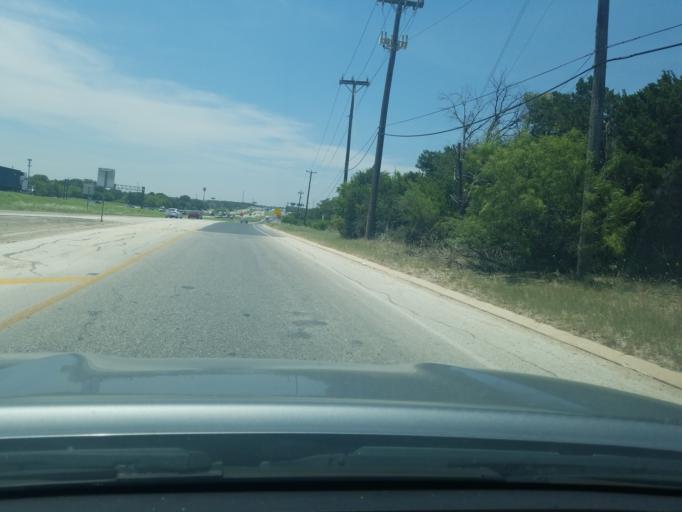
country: US
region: Texas
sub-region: Bexar County
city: Hollywood Park
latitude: 29.6020
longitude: -98.4081
